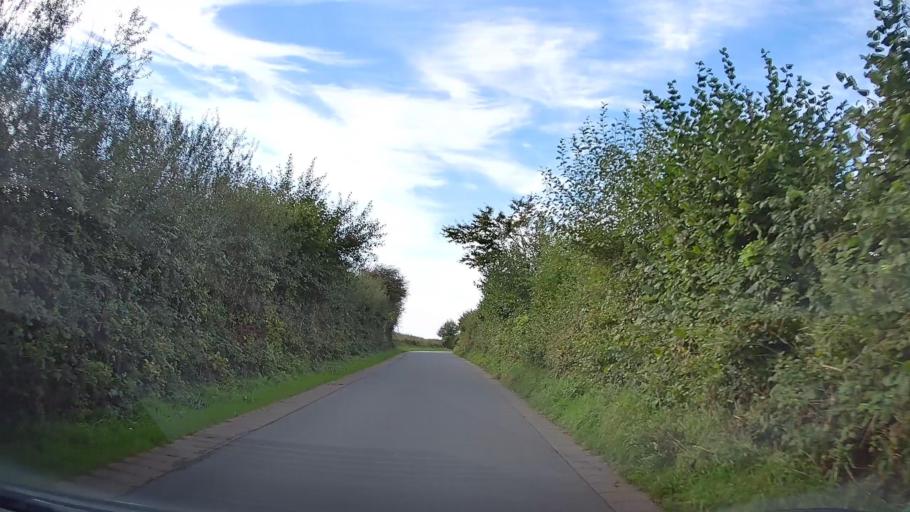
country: DE
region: Schleswig-Holstein
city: Ringsberg
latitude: 54.8230
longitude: 9.5985
